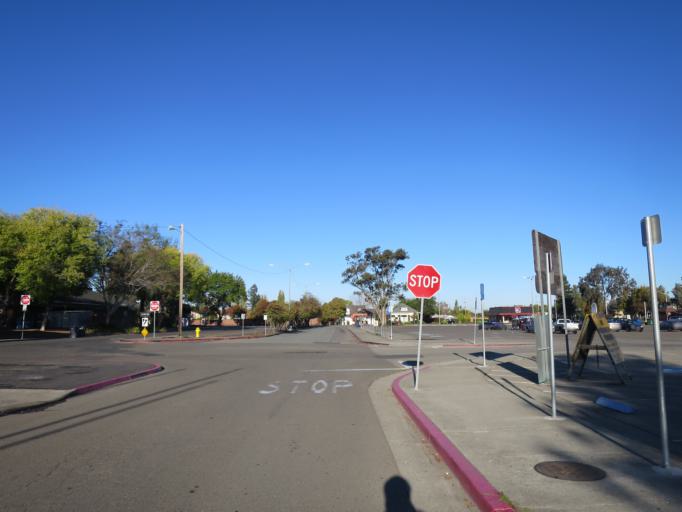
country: US
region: California
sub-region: Sonoma County
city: Petaluma
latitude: 38.2423
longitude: -122.6302
